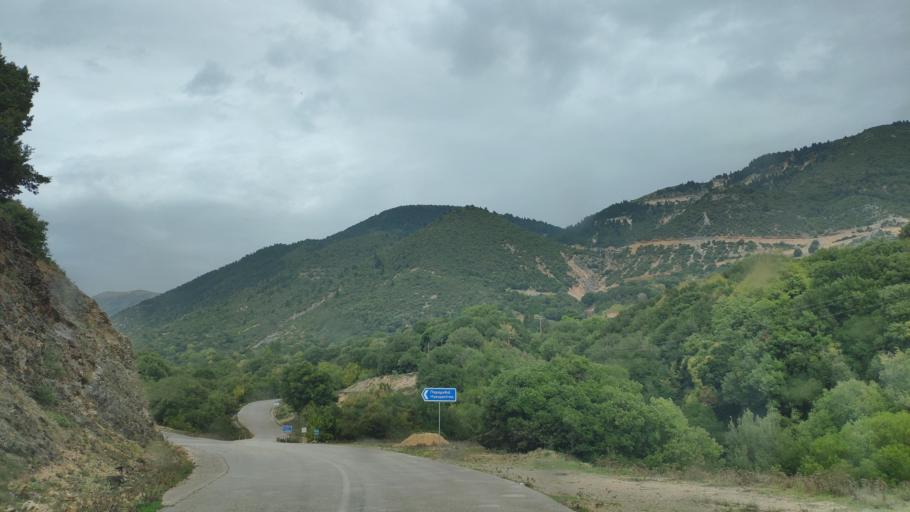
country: GR
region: Epirus
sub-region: Nomos Thesprotias
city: Paramythia
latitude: 39.4298
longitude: 20.6249
